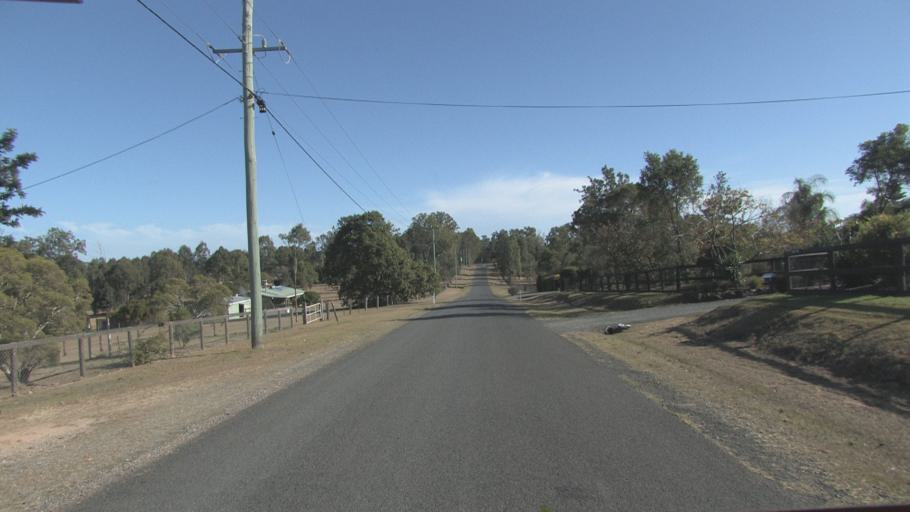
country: AU
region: Queensland
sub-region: Logan
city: Cedar Vale
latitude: -27.8352
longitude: 152.9931
